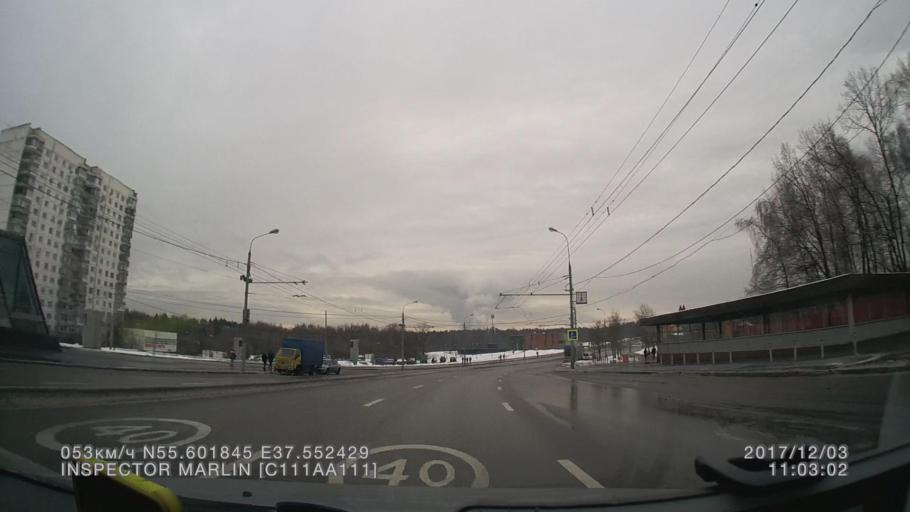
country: RU
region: Moscow
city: Yasenevo
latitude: 55.6018
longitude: 37.5525
